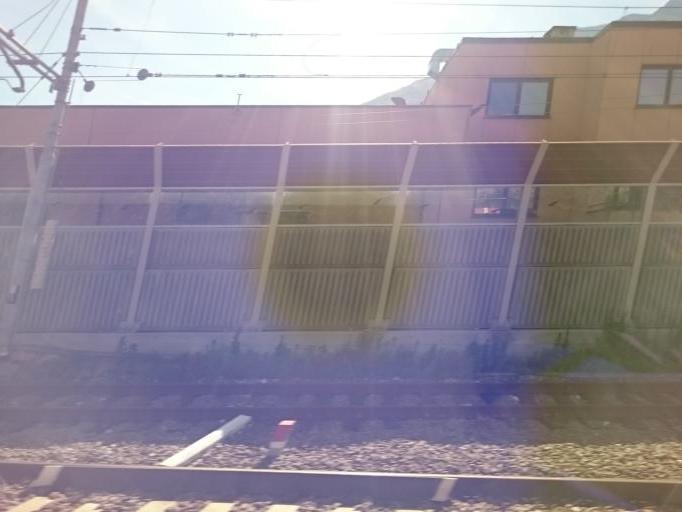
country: IT
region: Trentino-Alto Adige
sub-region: Provincia di Trento
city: Mattarello
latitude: 46.0021
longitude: 11.1242
